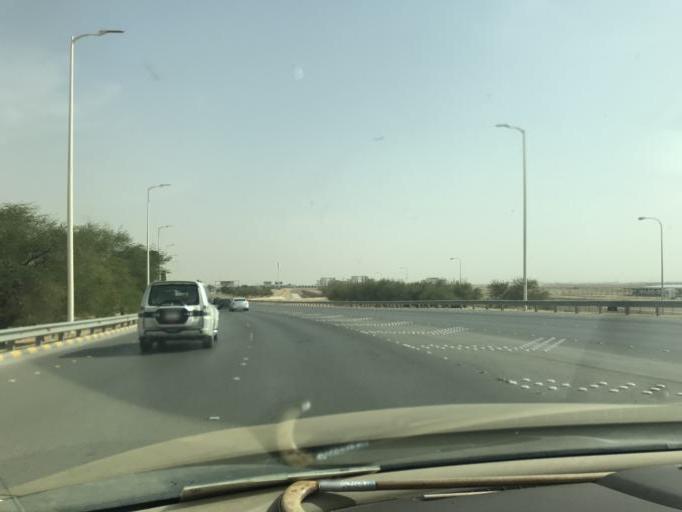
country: SA
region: Ar Riyad
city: Riyadh
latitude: 24.9432
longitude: 46.7064
